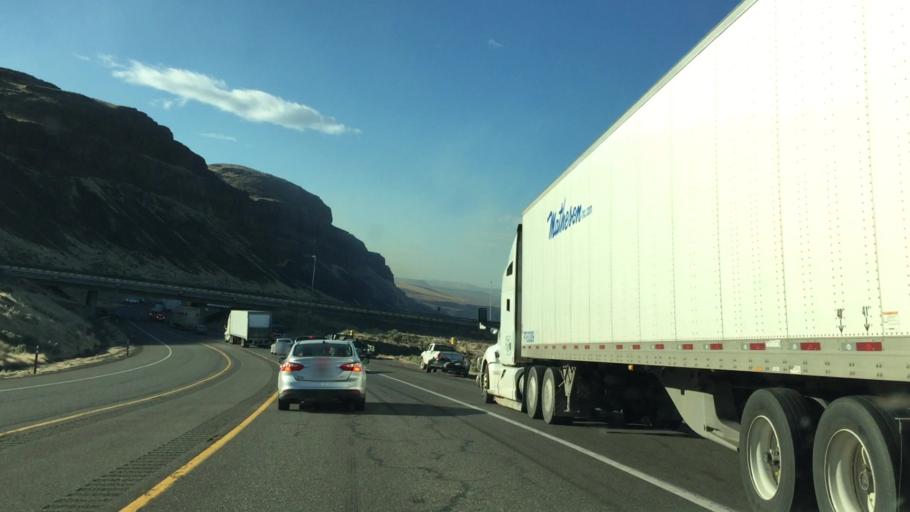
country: US
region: Washington
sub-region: Grant County
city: Mattawa
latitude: 46.9465
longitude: -119.9636
